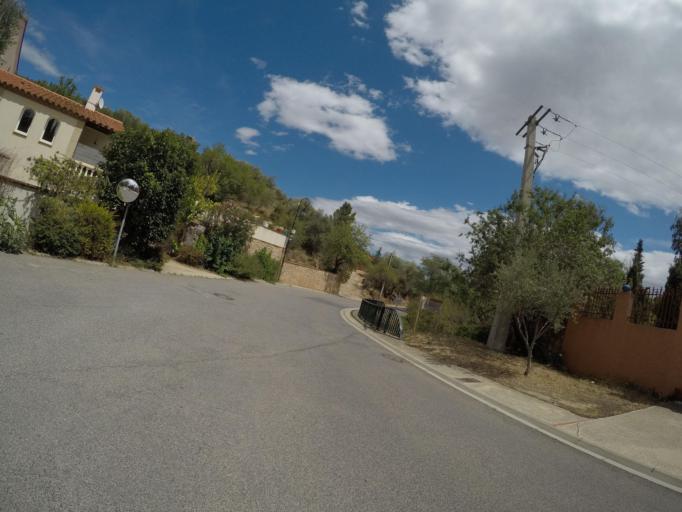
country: FR
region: Languedoc-Roussillon
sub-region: Departement des Pyrenees-Orientales
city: Baixas
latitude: 42.7582
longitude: 2.7569
